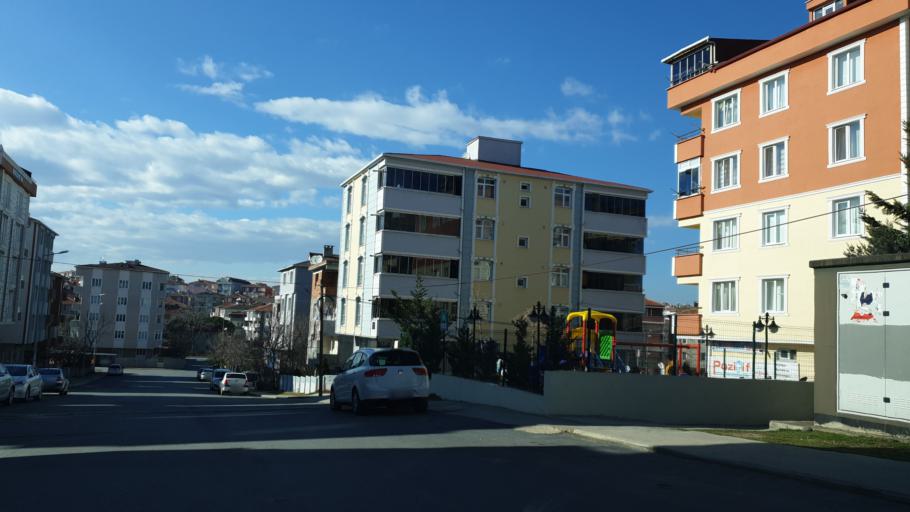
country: TR
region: Tekirdag
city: Cerkezkoey
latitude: 41.2861
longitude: 28.0078
